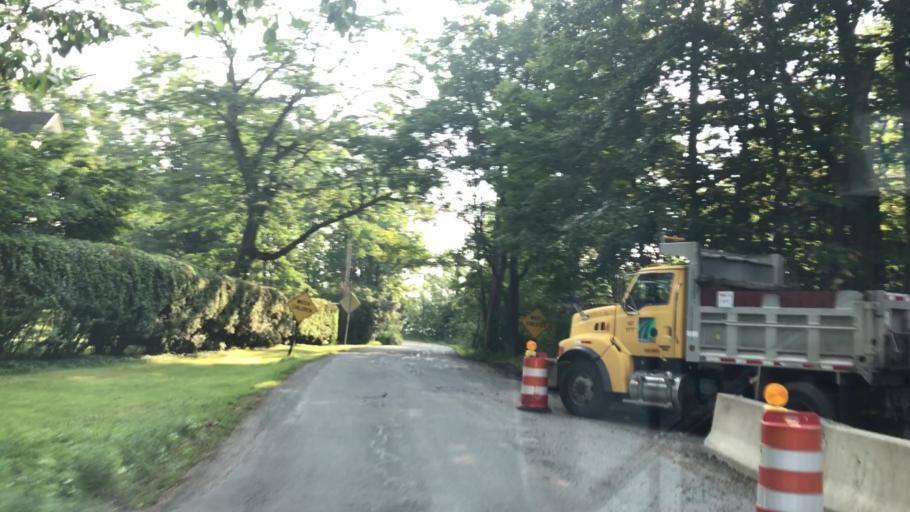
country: US
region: Pennsylvania
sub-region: Wyoming County
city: Factoryville
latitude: 41.6060
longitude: -75.7278
